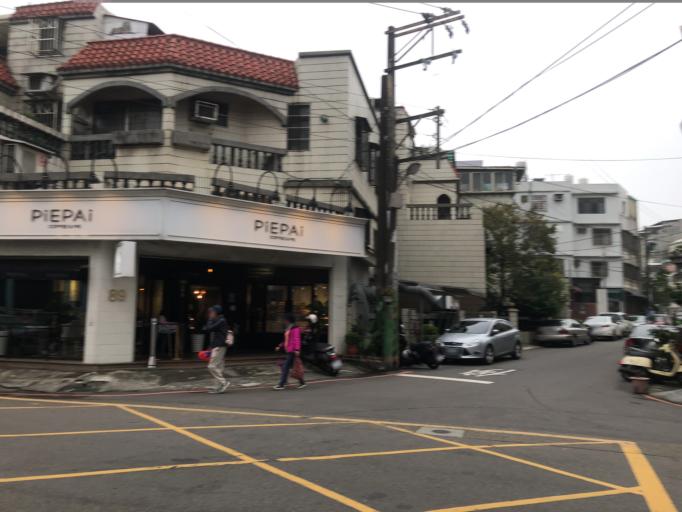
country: TW
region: Taiwan
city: Taoyuan City
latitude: 24.9517
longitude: 121.2365
